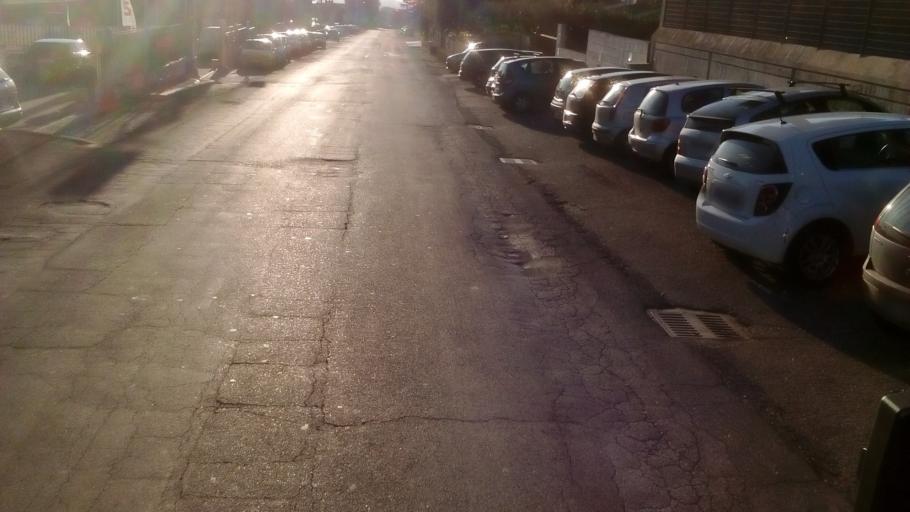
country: IT
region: Latium
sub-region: Citta metropolitana di Roma Capitale
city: Albano Laziale
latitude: 41.7128
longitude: 12.6267
